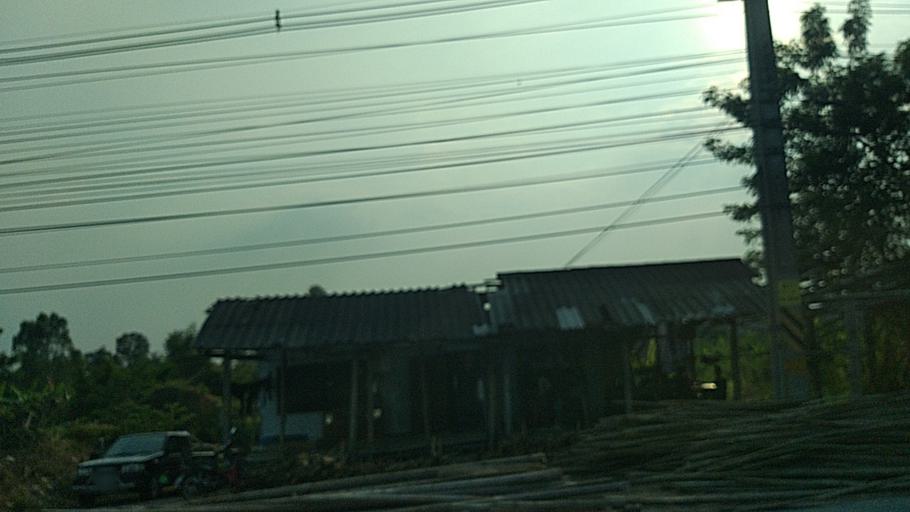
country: TH
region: Nakhon Nayok
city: Nakhon Nayok
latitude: 14.2052
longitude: 101.1876
